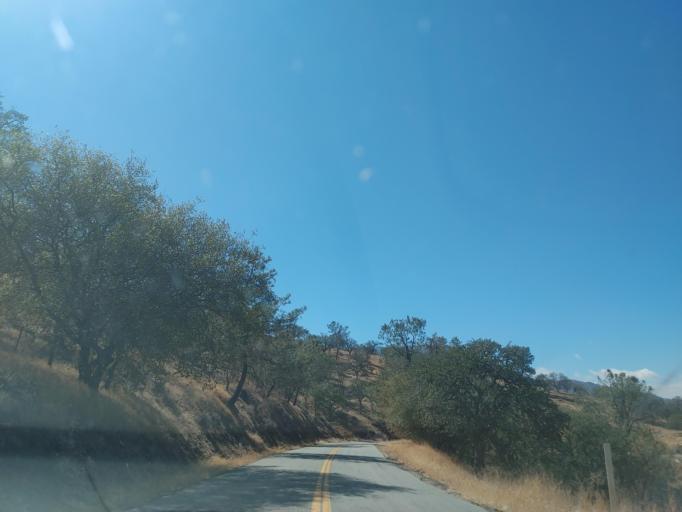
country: US
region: California
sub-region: Kern County
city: Golden Hills
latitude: 35.1931
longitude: -118.5264
